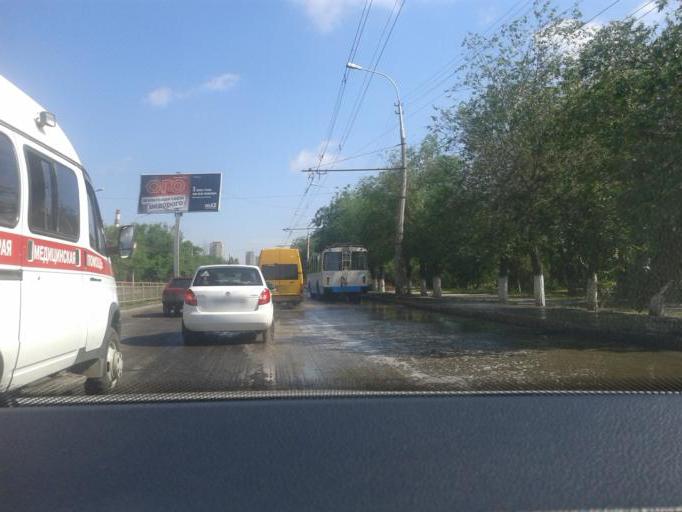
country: RU
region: Volgograd
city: Volgograd
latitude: 48.6072
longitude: 44.4223
